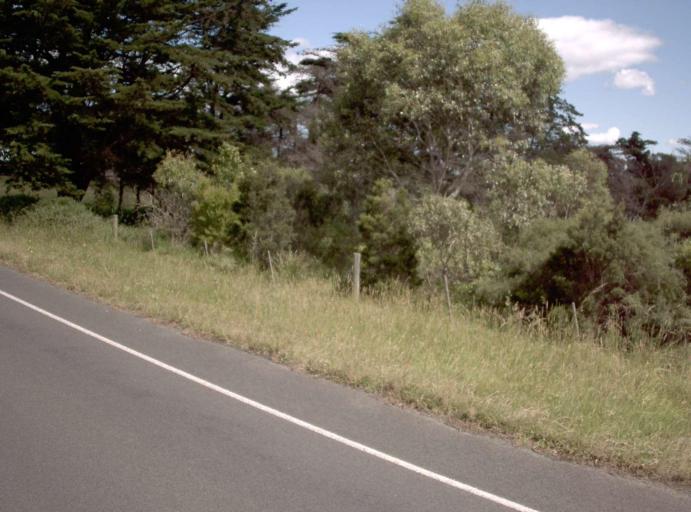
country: AU
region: Victoria
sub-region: Bass Coast
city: Phillip Island
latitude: -38.4967
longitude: 145.2066
